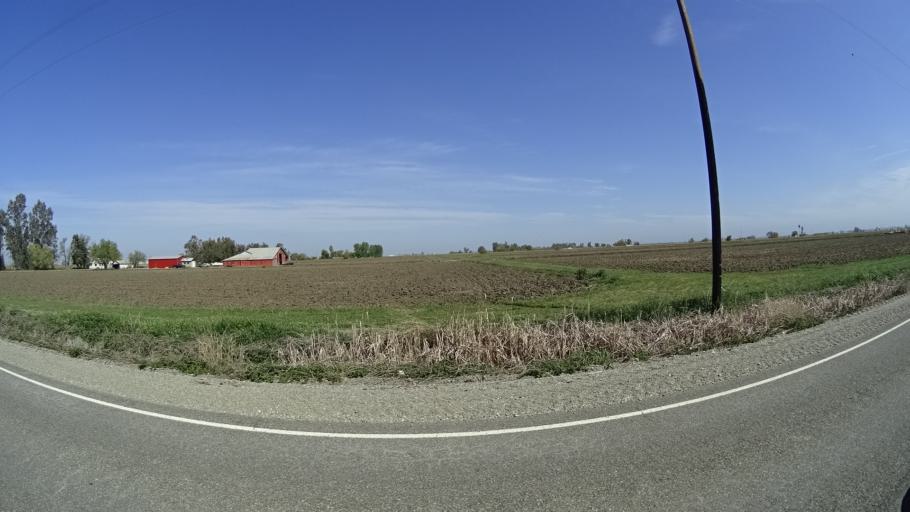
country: US
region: California
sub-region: Glenn County
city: Willows
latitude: 39.5825
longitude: -122.0629
